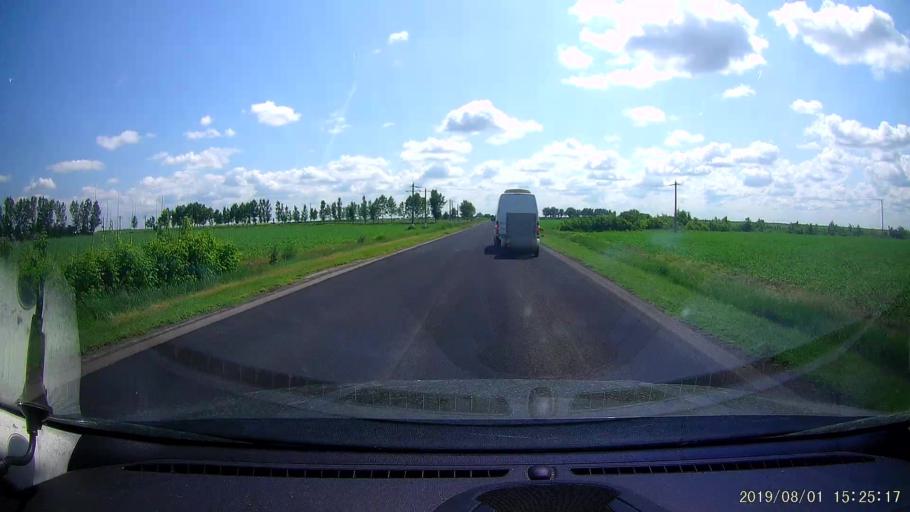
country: RO
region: Braila
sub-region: Comuna Viziru
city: Lanurile
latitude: 45.0241
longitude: 27.7379
